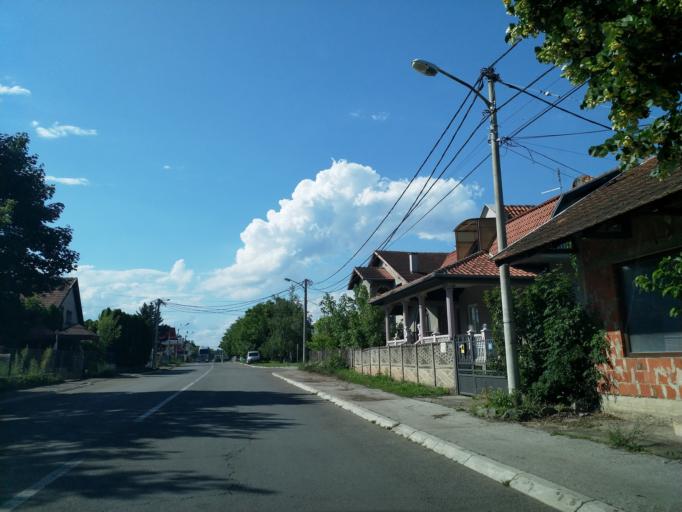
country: RS
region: Central Serbia
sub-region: Pomoravski Okrug
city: Paracin
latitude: 43.8496
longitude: 21.4116
